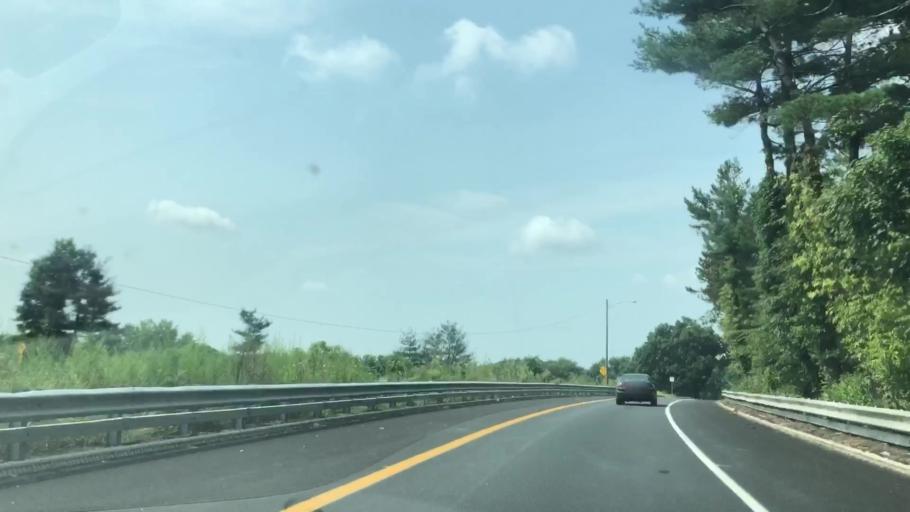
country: US
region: New Jersey
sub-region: Essex County
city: Westville
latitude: 40.8601
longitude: -74.3243
